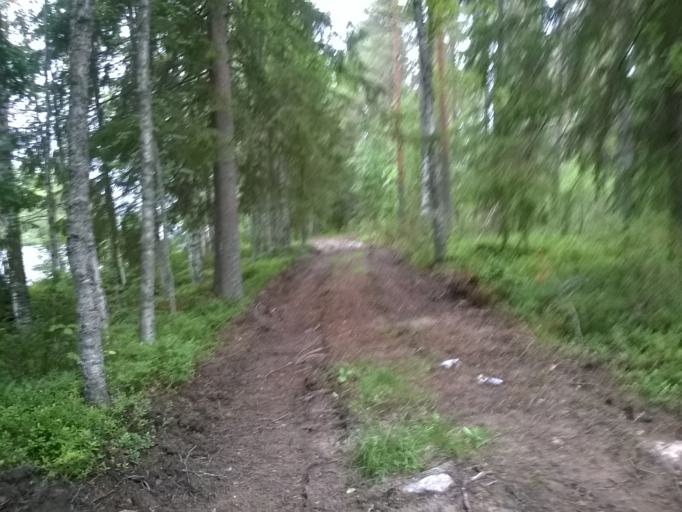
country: FI
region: Kainuu
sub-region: Kehys-Kainuu
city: Kuhmo
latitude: 64.1253
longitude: 29.4014
